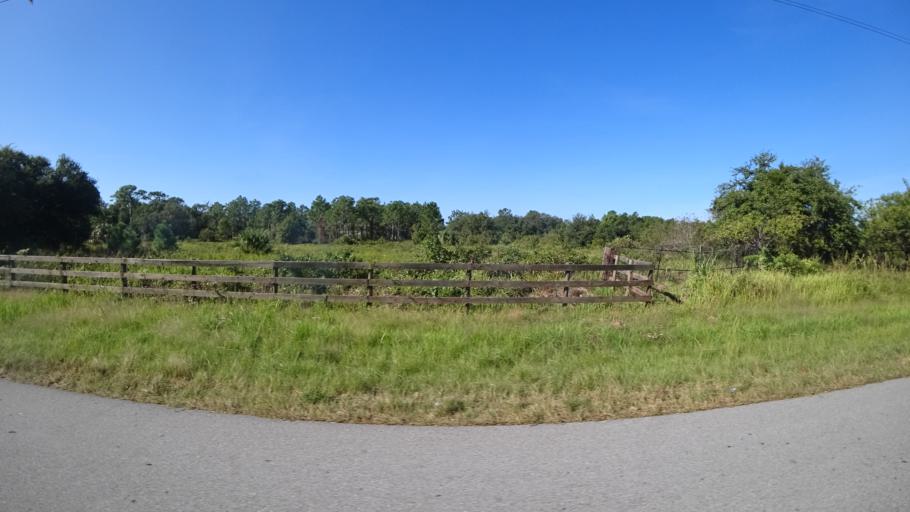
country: US
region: Florida
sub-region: Hillsborough County
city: Sun City Center
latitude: 27.6615
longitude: -82.3580
